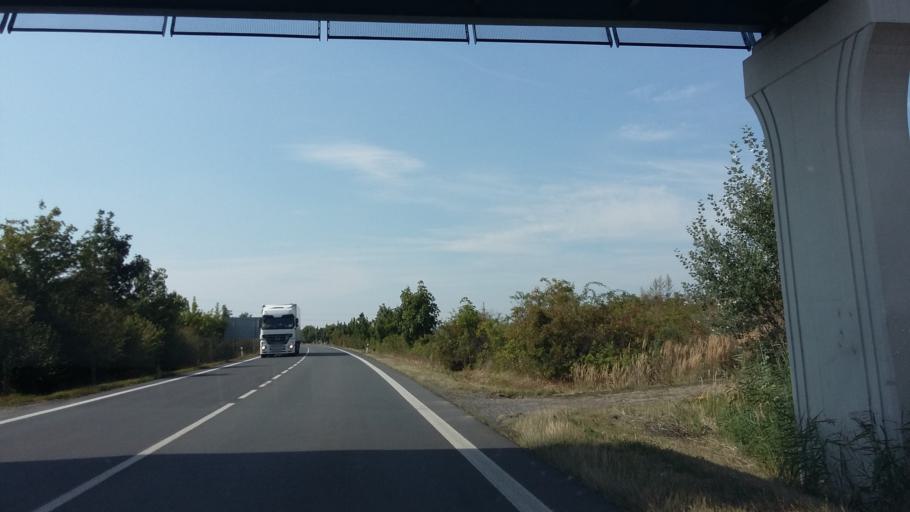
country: CZ
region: Central Bohemia
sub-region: Okres Kolin
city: Kolin
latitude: 50.0597
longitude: 15.2254
